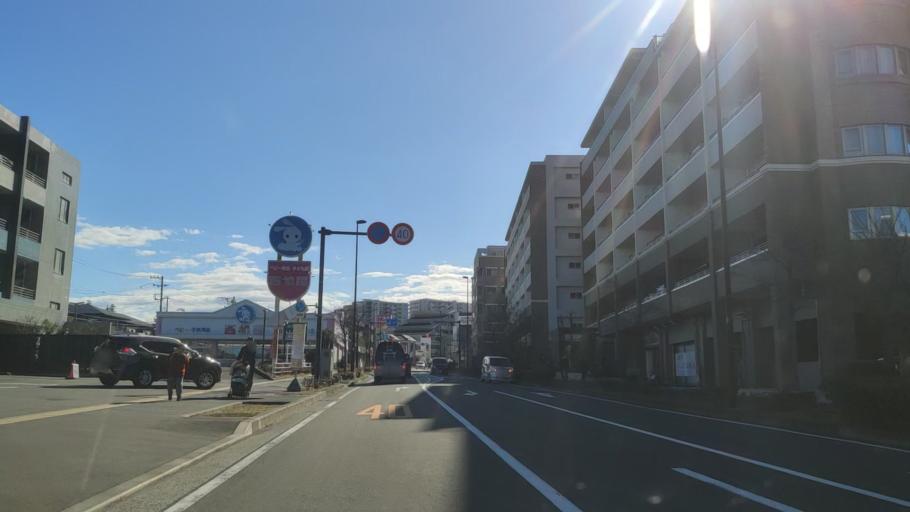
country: JP
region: Tokyo
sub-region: Machida-shi
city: Machida
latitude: 35.5242
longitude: 139.4984
